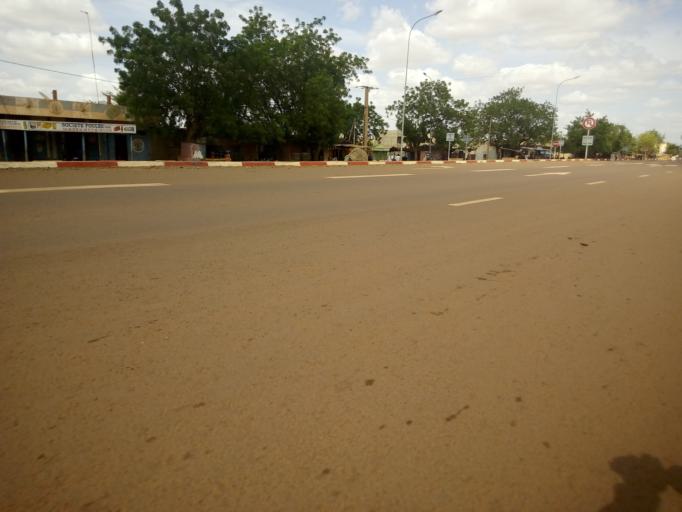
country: ML
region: Segou
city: Segou
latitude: 13.4296
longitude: -6.2233
